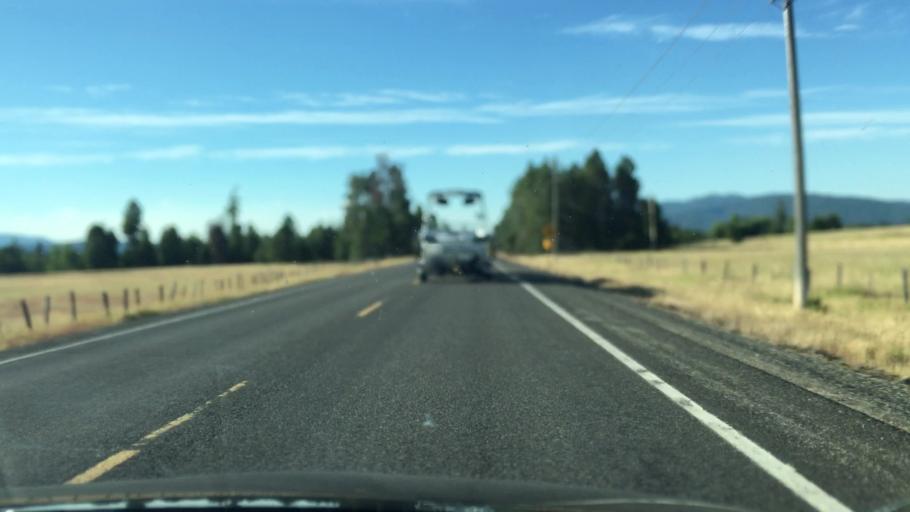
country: US
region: Idaho
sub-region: Valley County
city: Cascade
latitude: 44.4526
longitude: -115.9994
